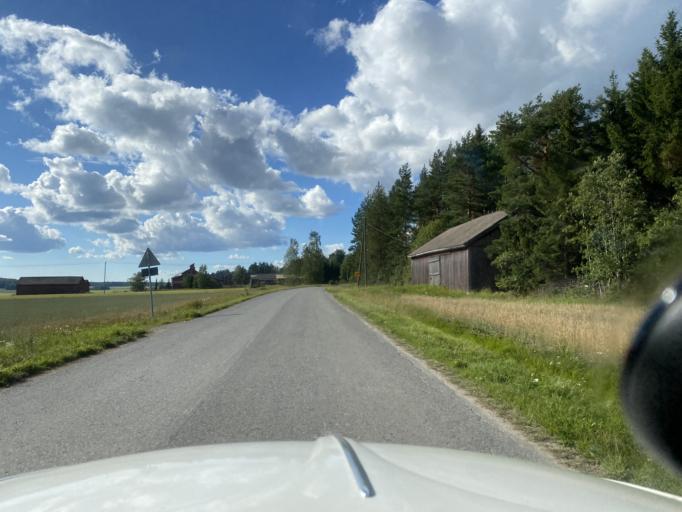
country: FI
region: Pirkanmaa
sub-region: Lounais-Pirkanmaa
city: Punkalaidun
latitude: 61.1444
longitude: 23.1995
